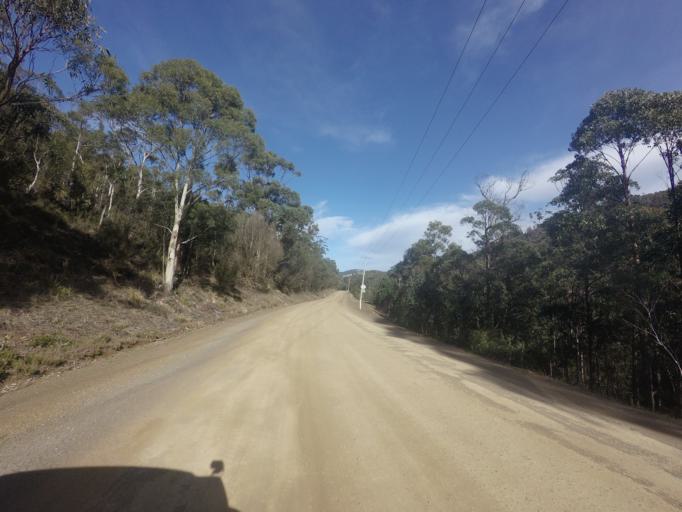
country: AU
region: Tasmania
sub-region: Huon Valley
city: Huonville
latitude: -43.0566
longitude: 147.0982
